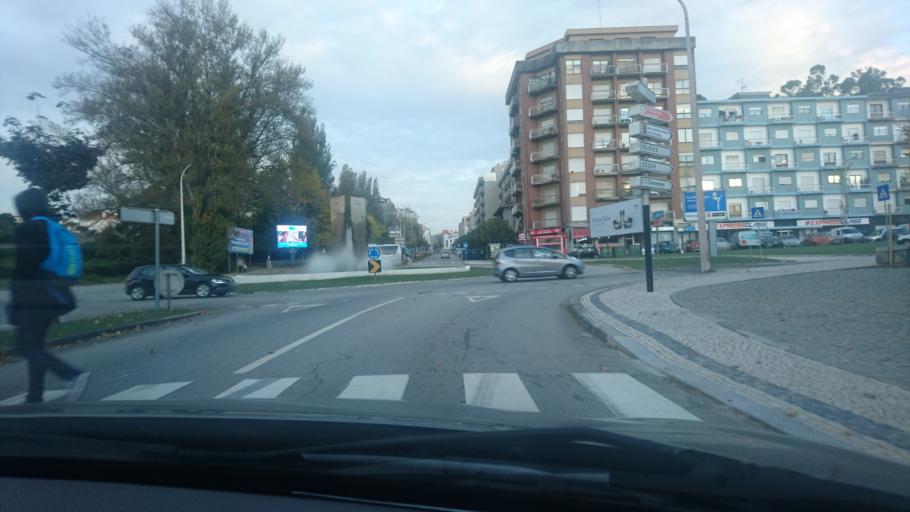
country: PT
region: Aveiro
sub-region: Sao Joao da Madeira
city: Sao Joao da Madeira
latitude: 40.8952
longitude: -8.4846
